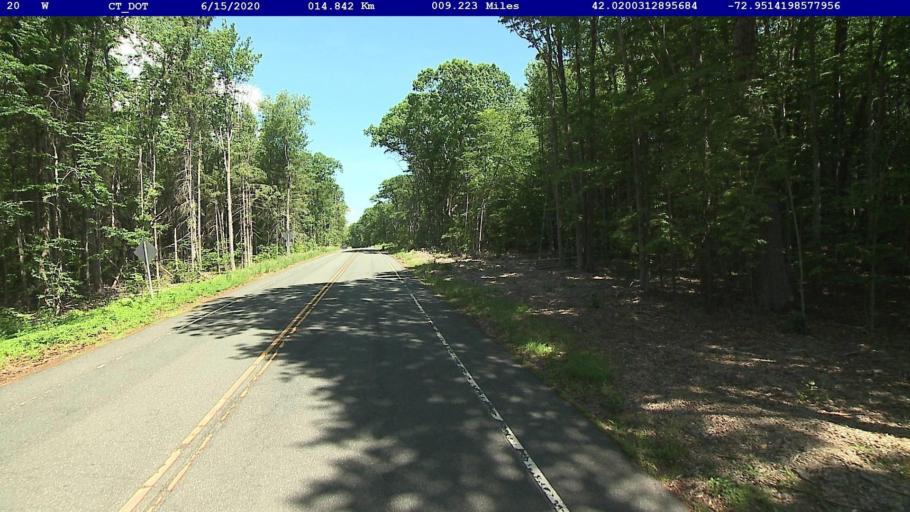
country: US
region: Massachusetts
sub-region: Hampden County
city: Granville
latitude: 42.0200
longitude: -72.9514
